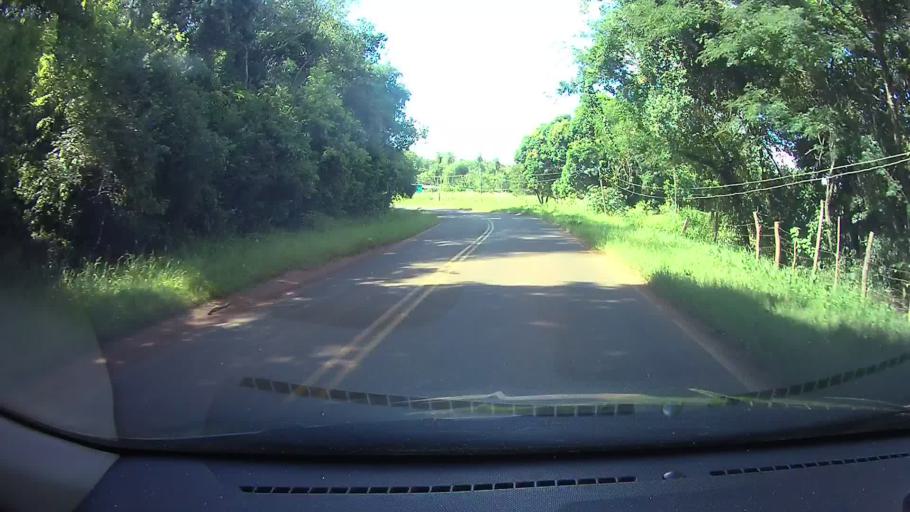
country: PY
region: Paraguari
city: Sapucai
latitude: -25.6619
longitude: -56.8566
